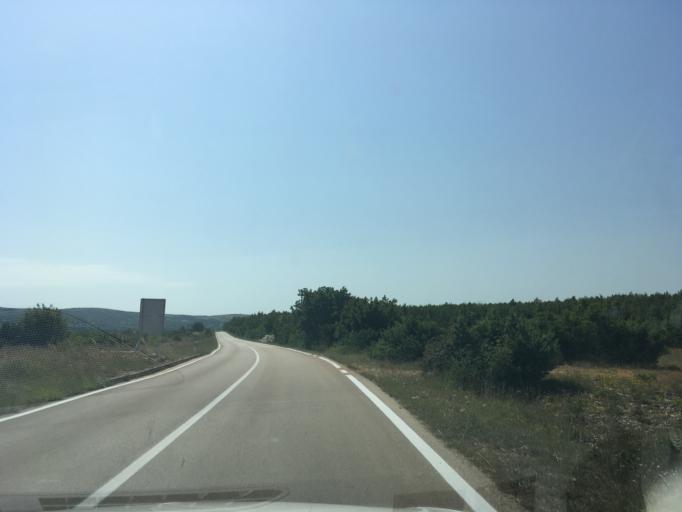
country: HR
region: Zadarska
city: Benkovac
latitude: 43.9654
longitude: 15.7395
